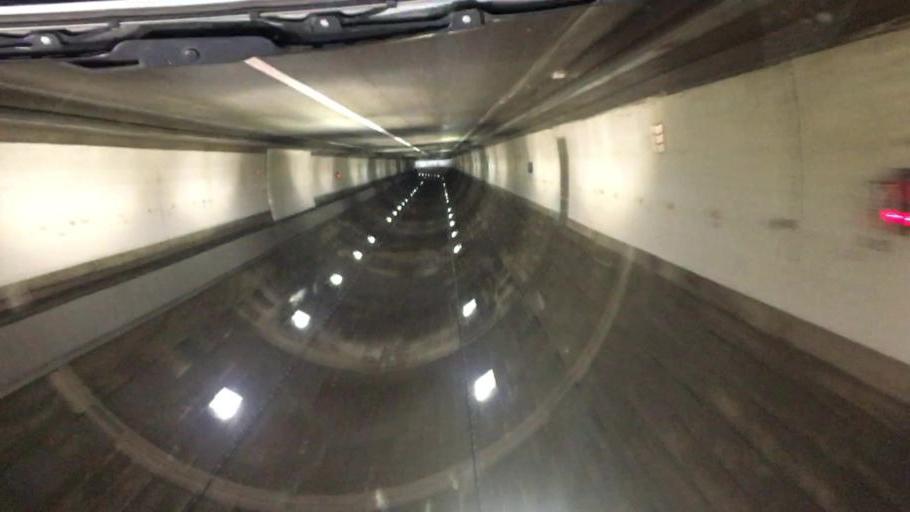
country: JP
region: Hokkaido
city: Otofuke
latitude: 43.3662
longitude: 143.2028
